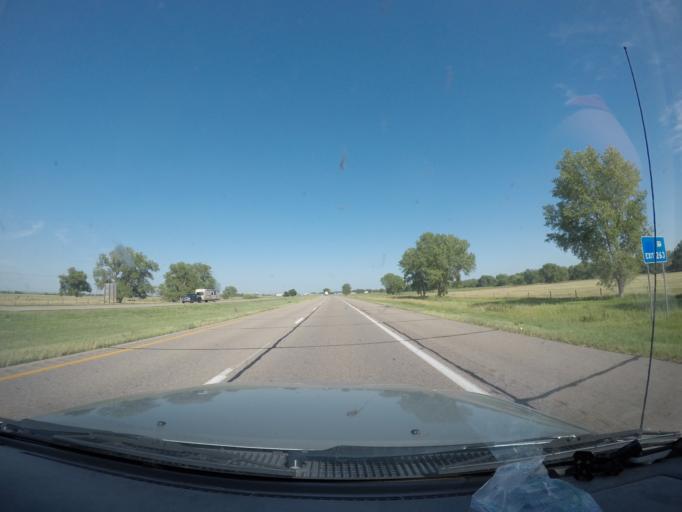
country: US
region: Nebraska
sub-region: Buffalo County
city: Kearney
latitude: 40.6779
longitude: -99.2755
